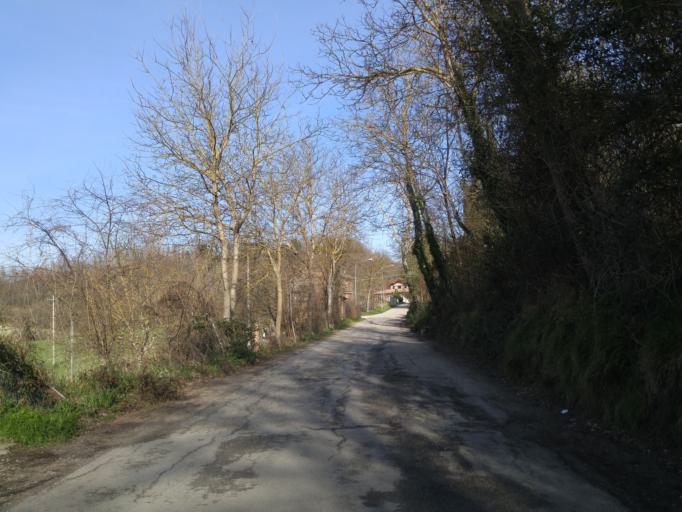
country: IT
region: The Marches
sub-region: Provincia di Pesaro e Urbino
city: Fermignano
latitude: 43.6796
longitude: 12.6487
